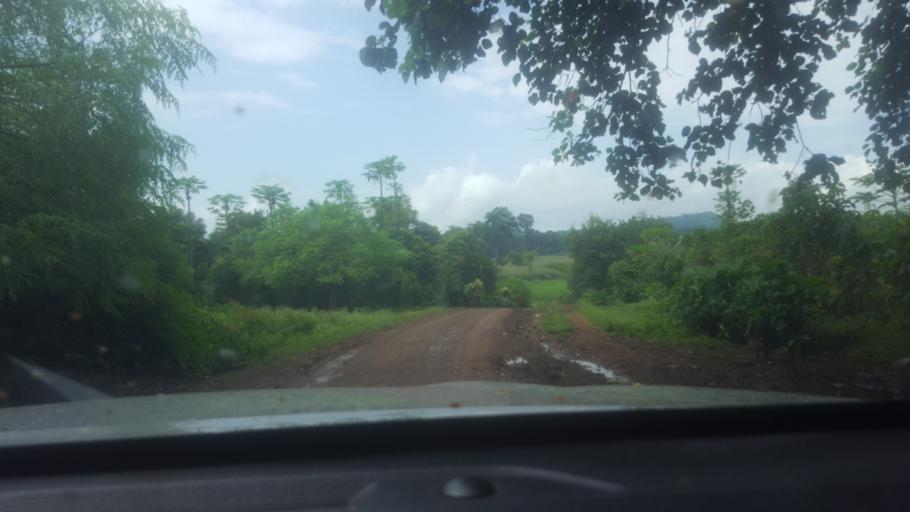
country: ET
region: Southern Nations, Nationalities, and People's Region
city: Tippi
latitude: 7.2760
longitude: 35.1496
